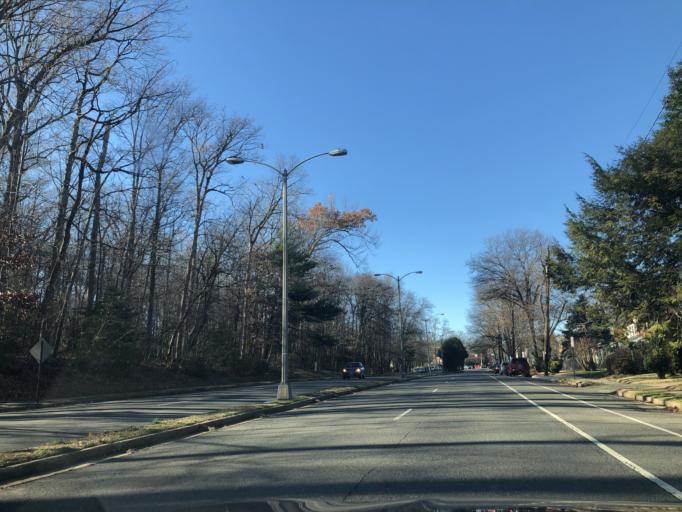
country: US
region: Virginia
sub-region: Arlington County
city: Arlington
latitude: 38.8835
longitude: -77.1244
